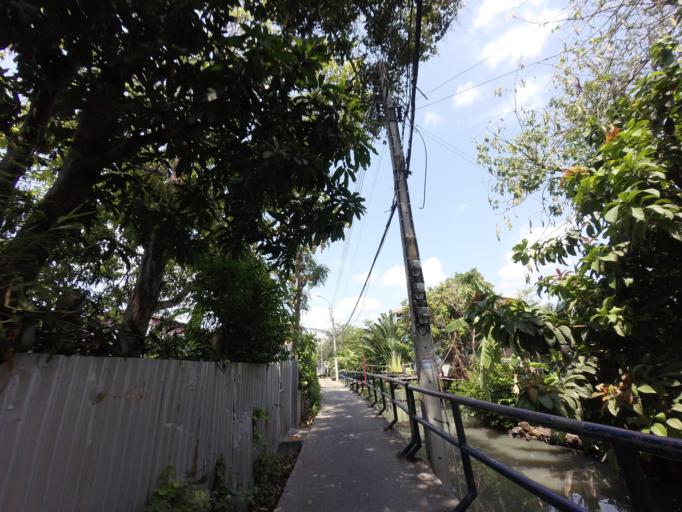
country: TH
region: Bangkok
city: Rat Burana
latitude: 13.6594
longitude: 100.5062
